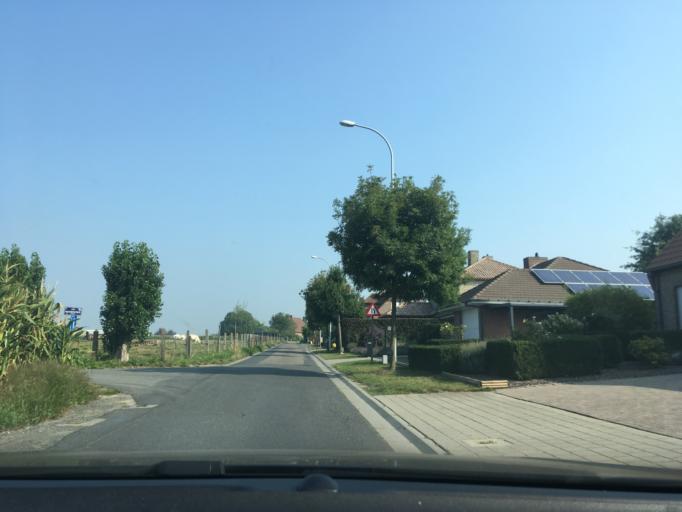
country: BE
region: Flanders
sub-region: Provincie West-Vlaanderen
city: Izegem
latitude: 50.9353
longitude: 3.1853
